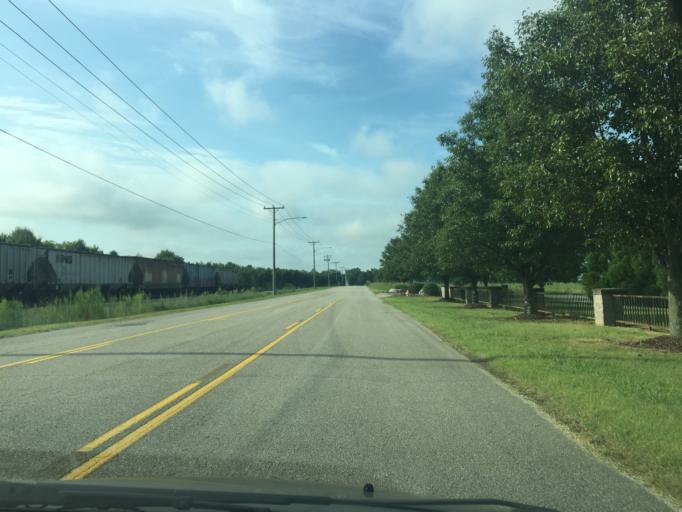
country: US
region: Tennessee
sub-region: Hamilton County
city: East Chattanooga
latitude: 35.0758
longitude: -85.2718
